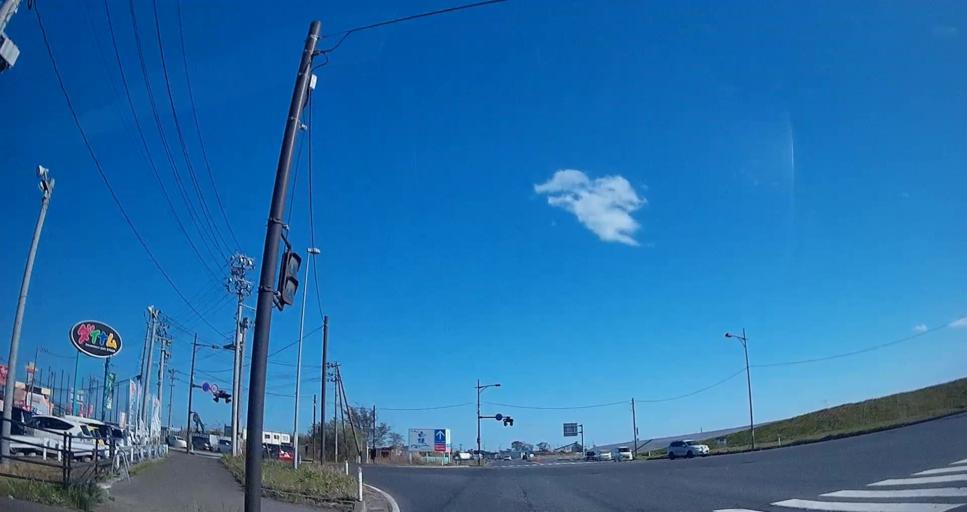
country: JP
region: Miyagi
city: Yamoto
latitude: 38.4315
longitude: 141.2486
